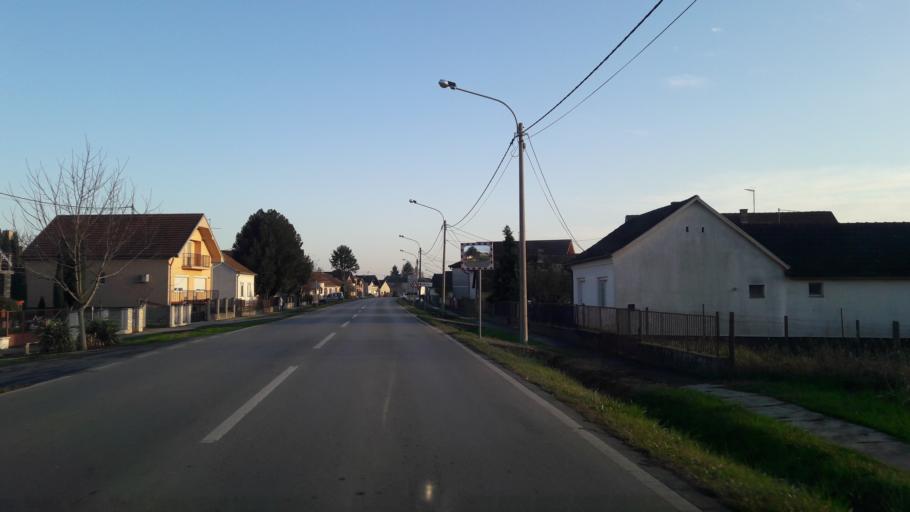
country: HR
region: Osjecko-Baranjska
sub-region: Grad Osijek
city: Bilje
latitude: 45.6095
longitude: 18.7397
